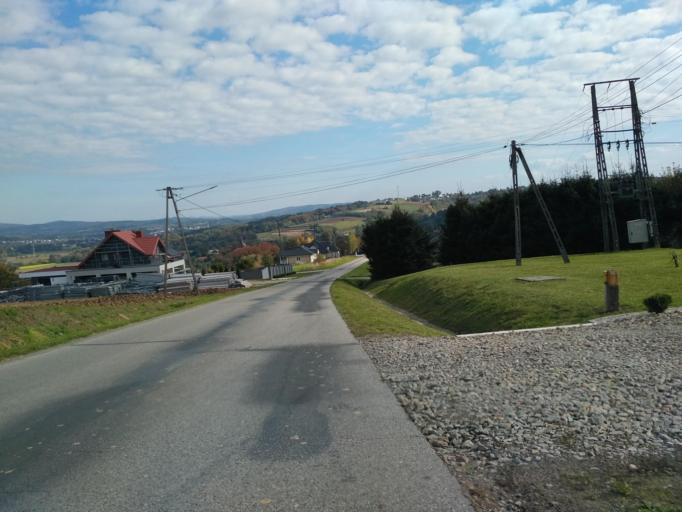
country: PL
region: Subcarpathian Voivodeship
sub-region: Powiat debicki
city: Brzostek
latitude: 49.8886
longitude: 21.3553
